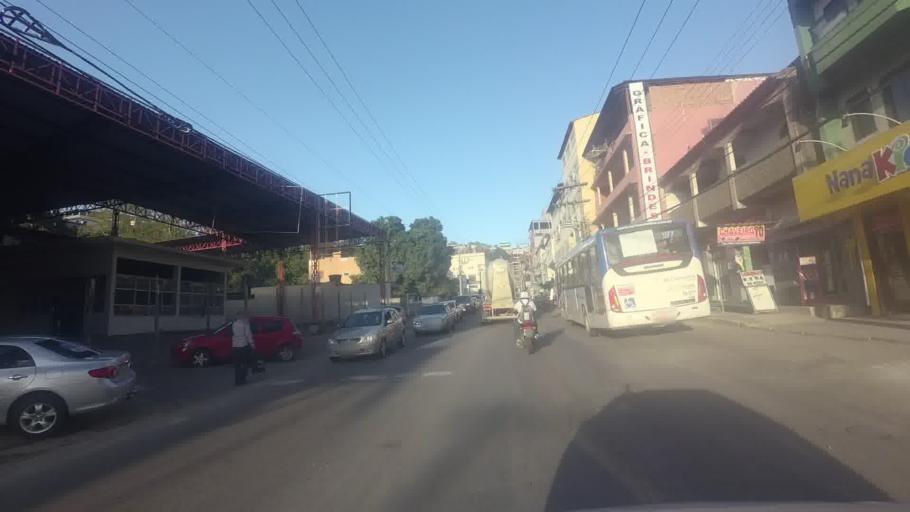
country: BR
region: Espirito Santo
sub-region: Cachoeiro De Itapemirim
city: Cachoeiro de Itapemirim
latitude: -20.8482
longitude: -41.1474
